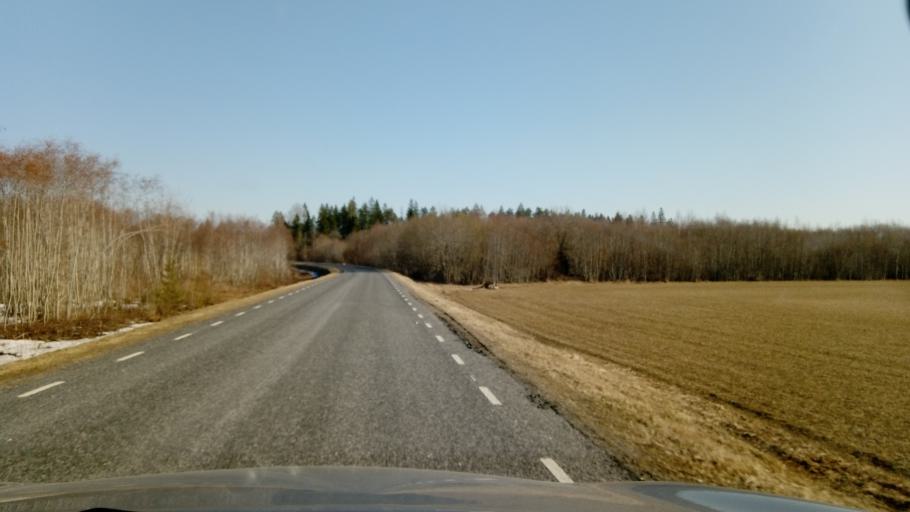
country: EE
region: Laeaene-Virumaa
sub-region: Tamsalu vald
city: Tamsalu
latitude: 59.1855
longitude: 26.1286
